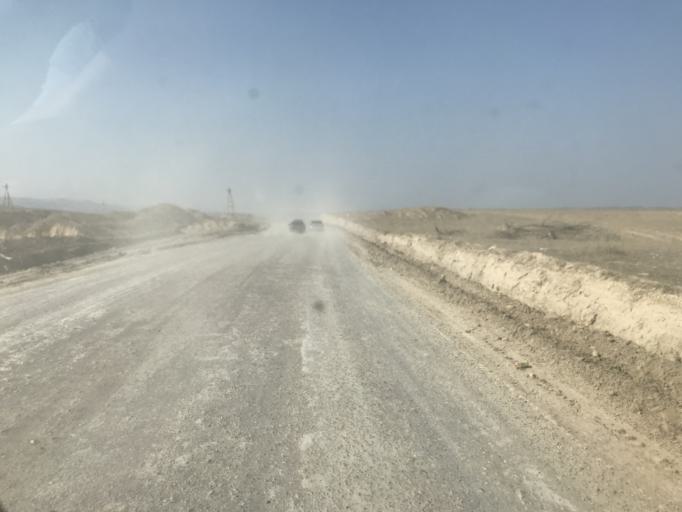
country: KG
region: Chuy
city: Bystrovka
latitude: 43.3221
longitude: 76.0472
